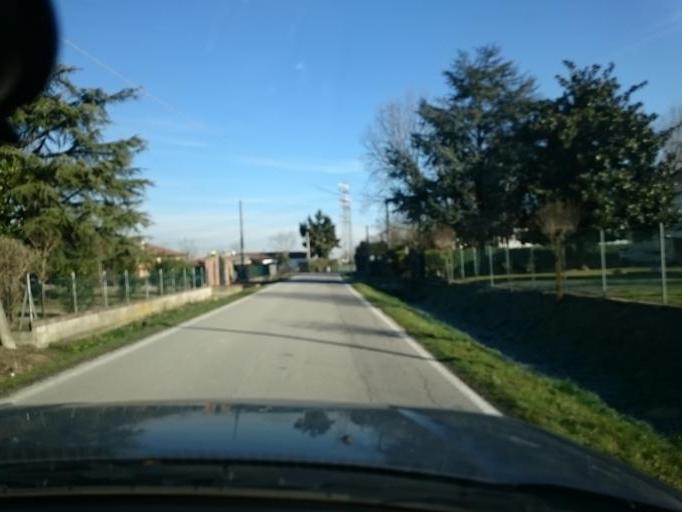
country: IT
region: Veneto
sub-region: Provincia di Venezia
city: Sambruson
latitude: 45.4182
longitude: 12.1059
